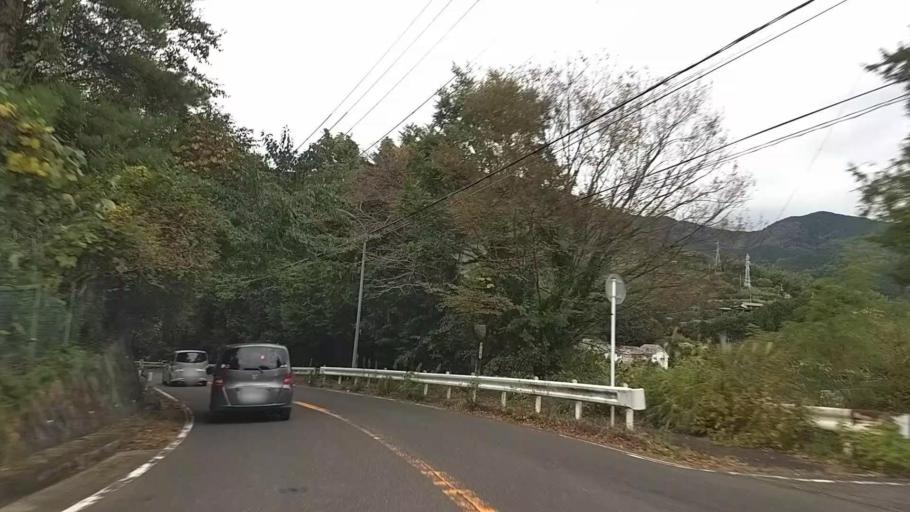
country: JP
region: Kanagawa
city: Odawara
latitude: 35.1981
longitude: 139.1330
